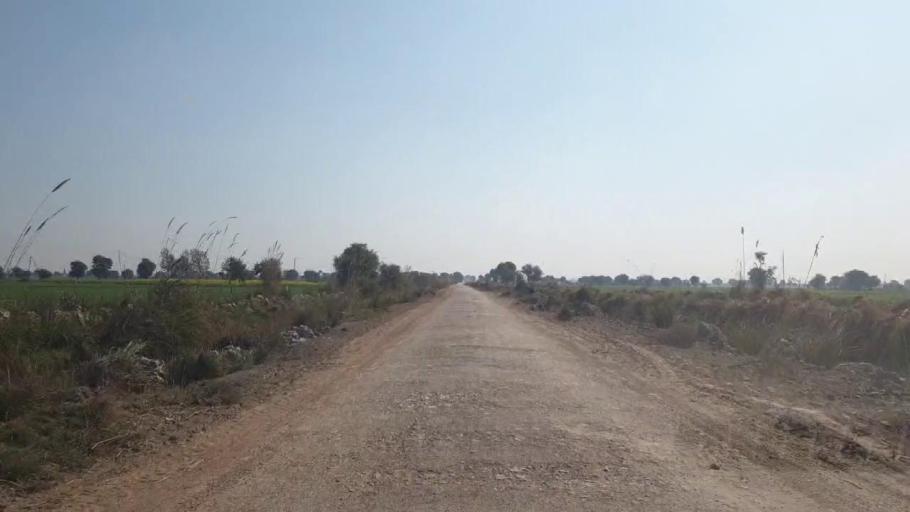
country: PK
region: Sindh
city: Shahdadpur
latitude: 25.9535
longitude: 68.6291
